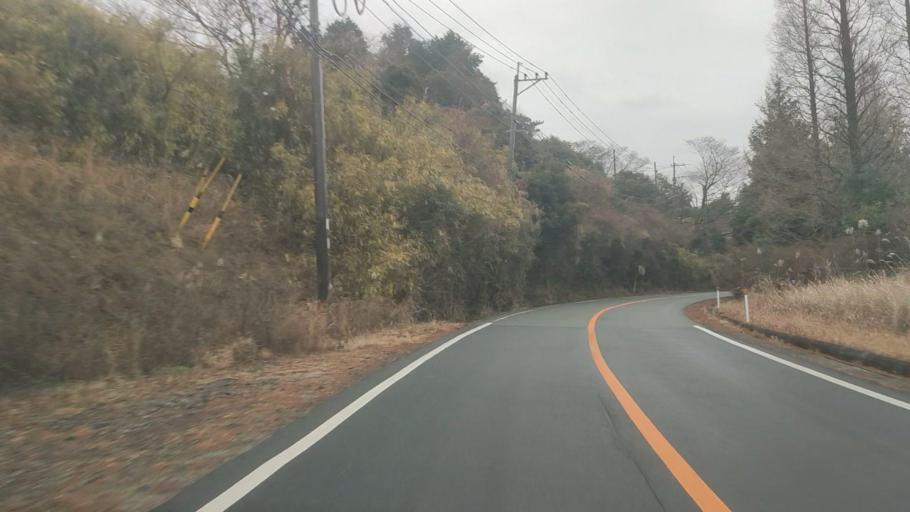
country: JP
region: Kumamoto
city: Aso
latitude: 32.8985
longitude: 131.0179
